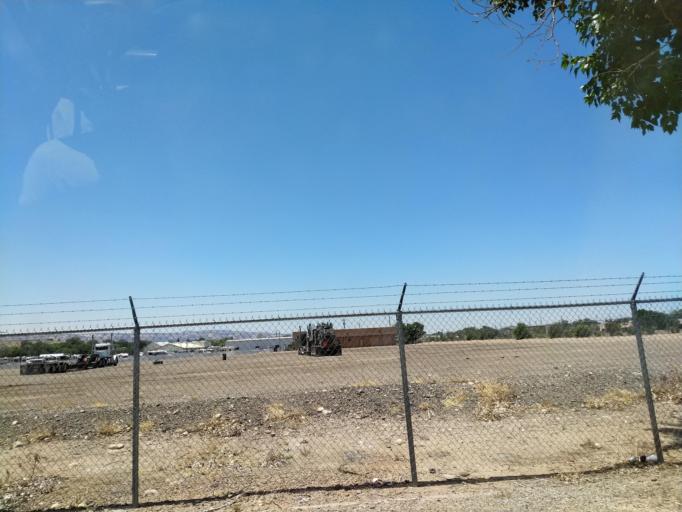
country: US
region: Colorado
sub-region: Mesa County
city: Orchard Mesa
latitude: 39.0383
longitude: -108.5399
